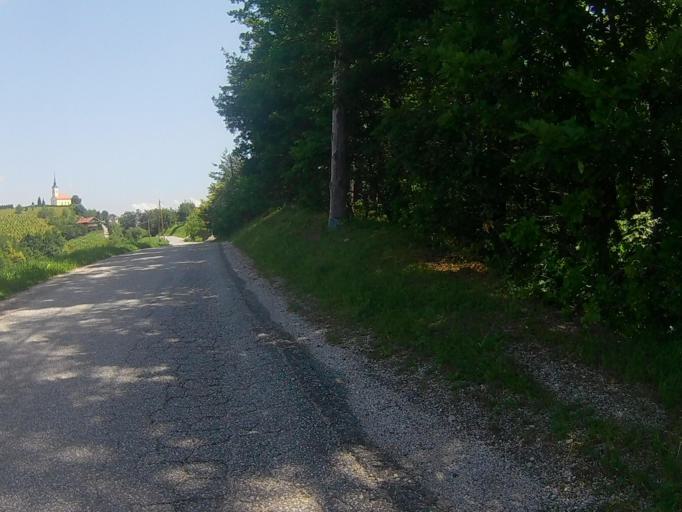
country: SI
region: Maribor
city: Kamnica
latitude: 46.5997
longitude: 15.6029
